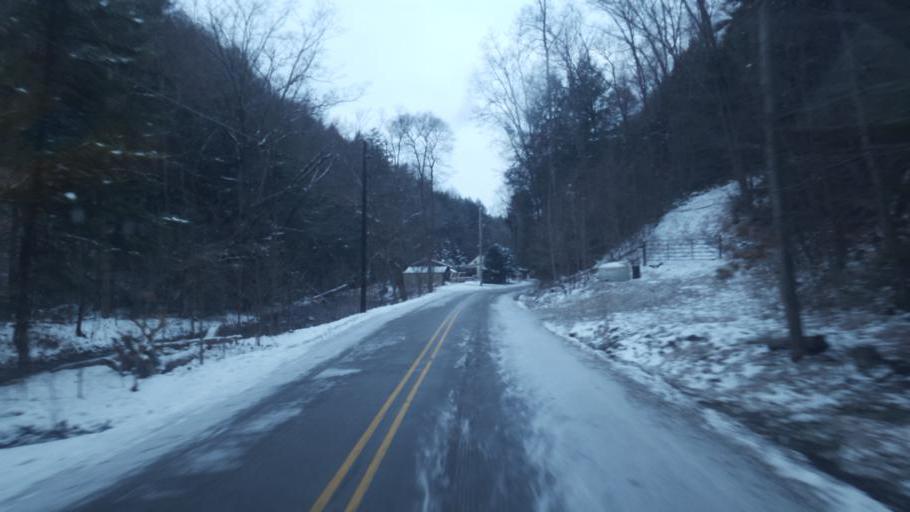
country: US
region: Pennsylvania
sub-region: Venango County
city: Sugarcreek
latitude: 41.4285
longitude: -79.9689
